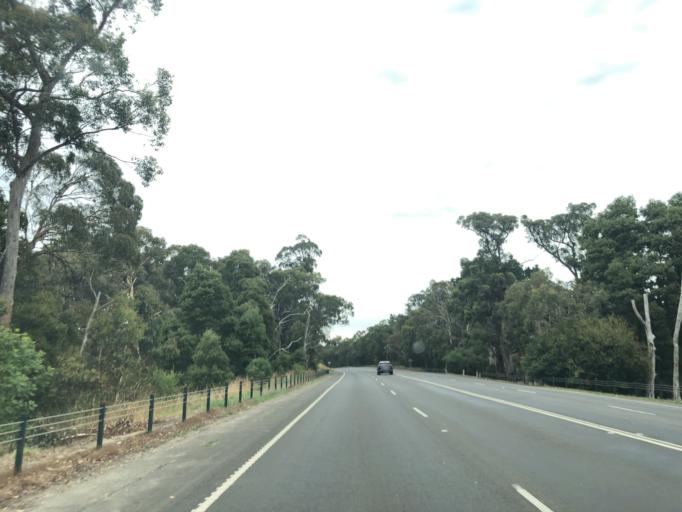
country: AU
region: Victoria
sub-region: Hume
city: Sunbury
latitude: -37.3829
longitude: 144.5270
